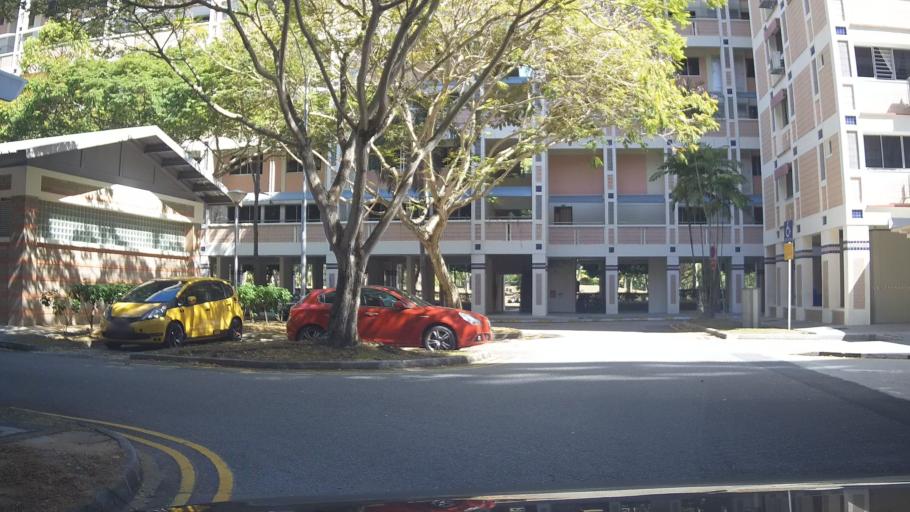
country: MY
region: Johor
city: Kampung Pasir Gudang Baru
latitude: 1.3685
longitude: 103.9537
